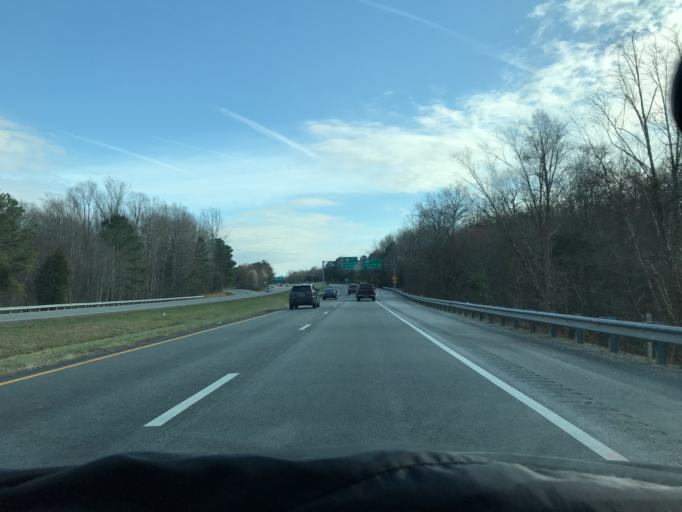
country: US
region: Virginia
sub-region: Chesterfield County
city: Brandermill
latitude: 37.4294
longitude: -77.6330
